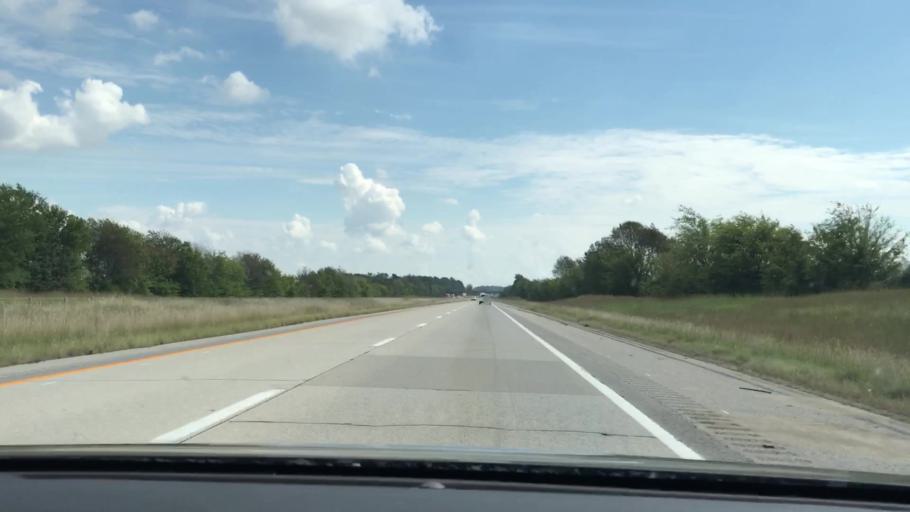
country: US
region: Kentucky
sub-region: Christian County
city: Hopkinsville
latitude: 36.7920
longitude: -87.5969
